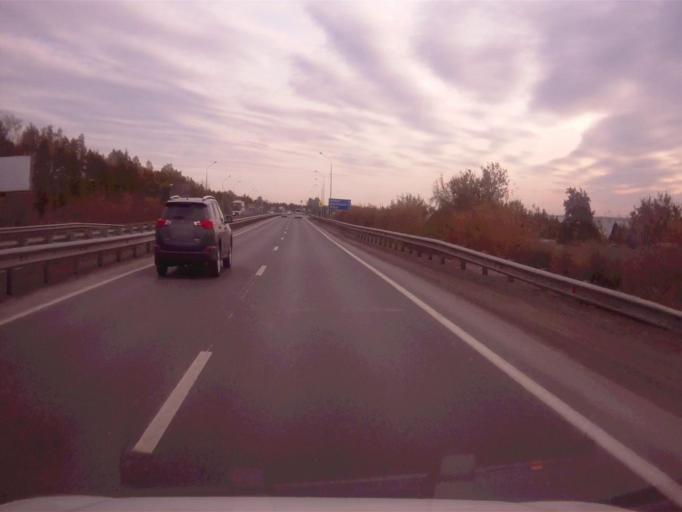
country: RU
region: Chelyabinsk
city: Novosineglazovskiy
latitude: 55.0341
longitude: 61.4431
